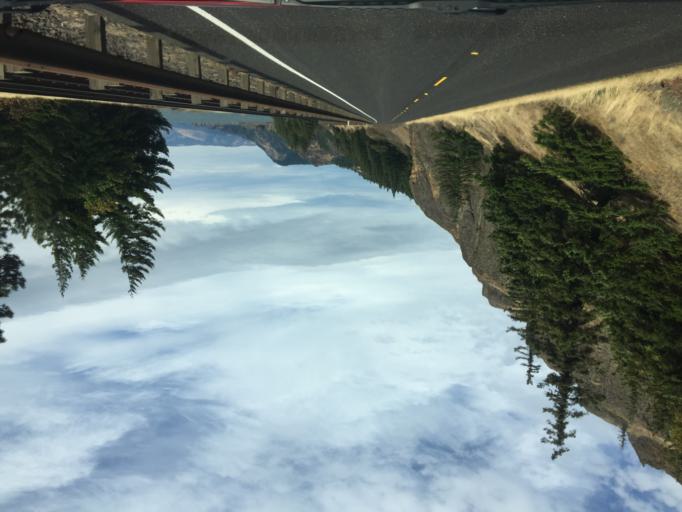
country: US
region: Washington
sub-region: Skamania County
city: Carson
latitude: 45.7032
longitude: -121.6930
